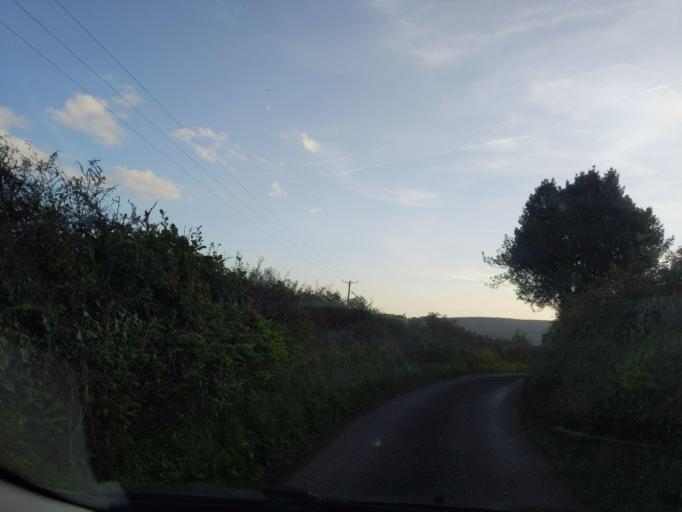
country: GB
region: England
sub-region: Devon
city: Bovey Tracey
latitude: 50.6219
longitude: -3.6929
